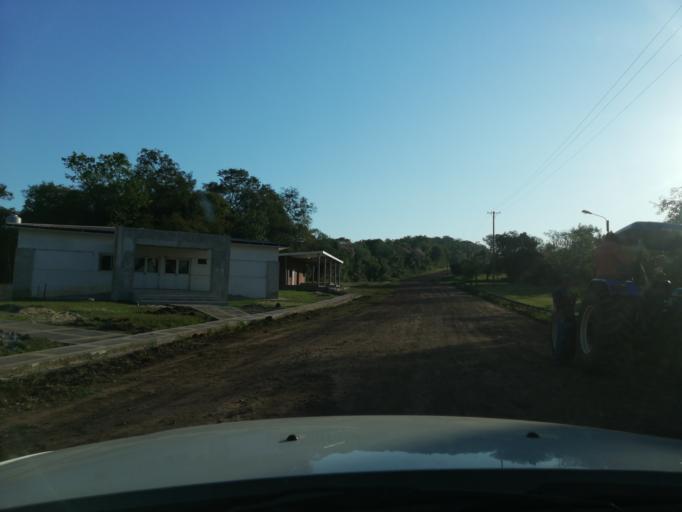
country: AR
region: Misiones
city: Cerro Cora
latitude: -27.6303
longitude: -55.7039
